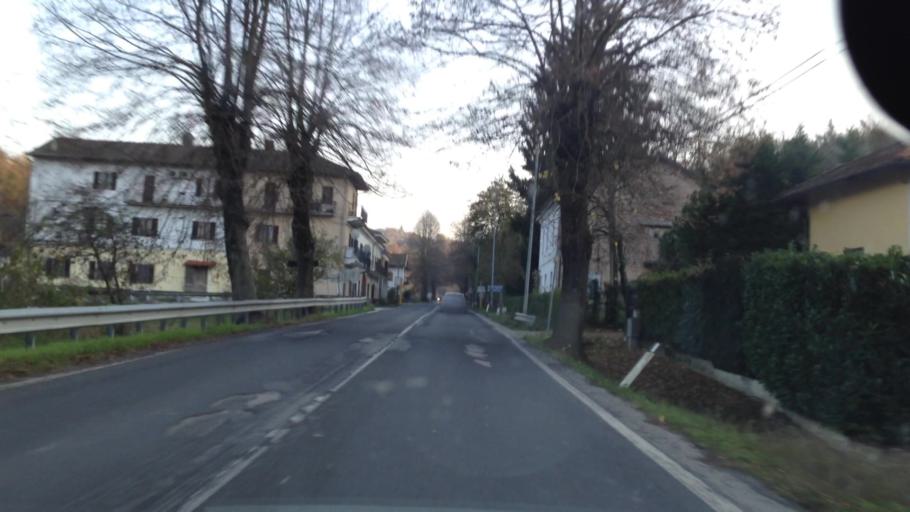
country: IT
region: Piedmont
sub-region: Provincia di Torino
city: Cavagnolo
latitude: 45.1332
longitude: 8.0565
